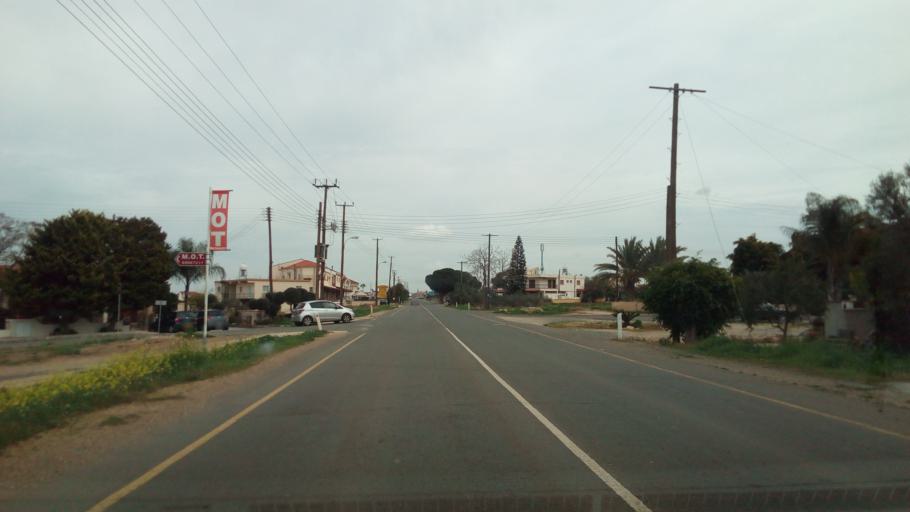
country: CY
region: Lefkosia
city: Astromeritis
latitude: 35.1375
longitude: 33.0400
